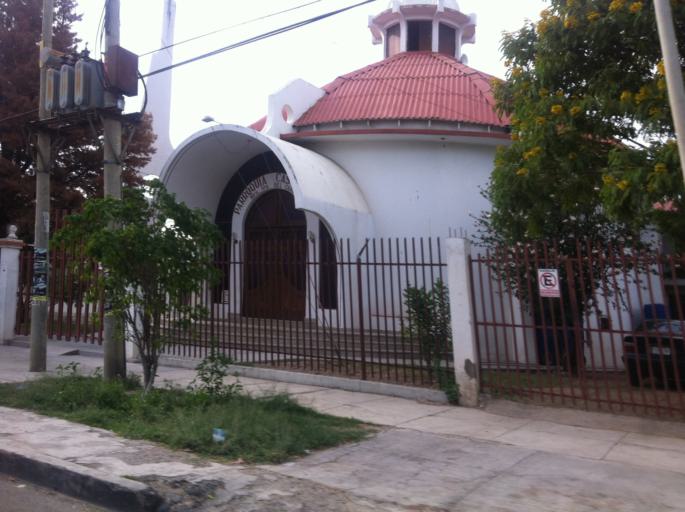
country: BO
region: Cochabamba
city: Cochabamba
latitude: -17.3796
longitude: -66.1446
